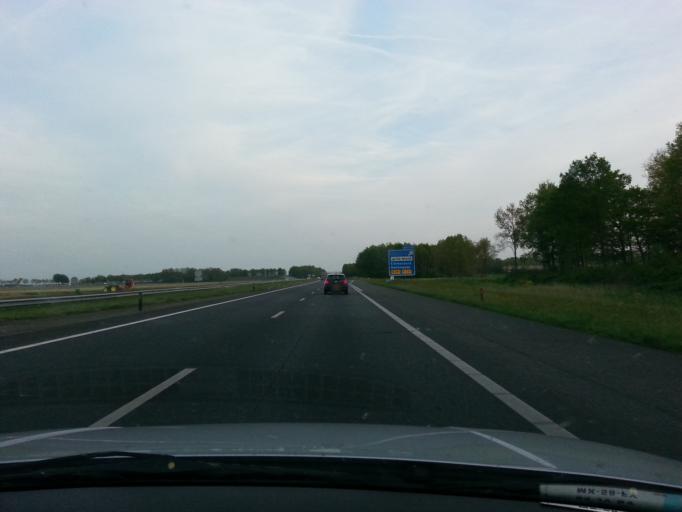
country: NL
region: Flevoland
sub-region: Gemeente Noordoostpolder
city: Emmeloord
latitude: 52.7339
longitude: 5.7693
